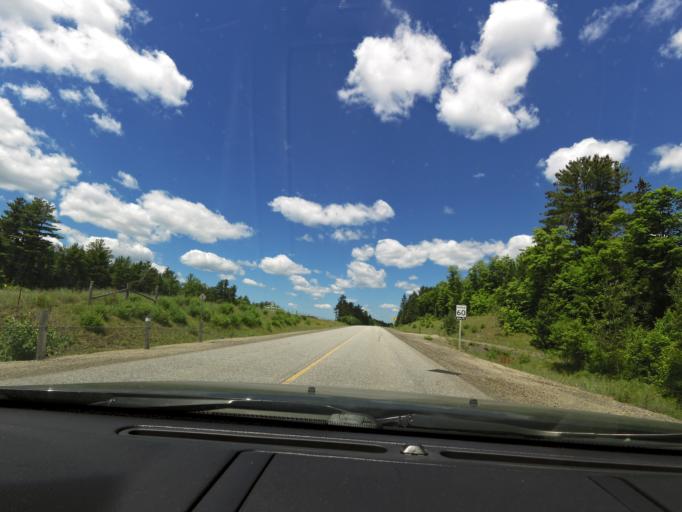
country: CA
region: Ontario
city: Huntsville
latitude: 45.5167
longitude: -79.3103
